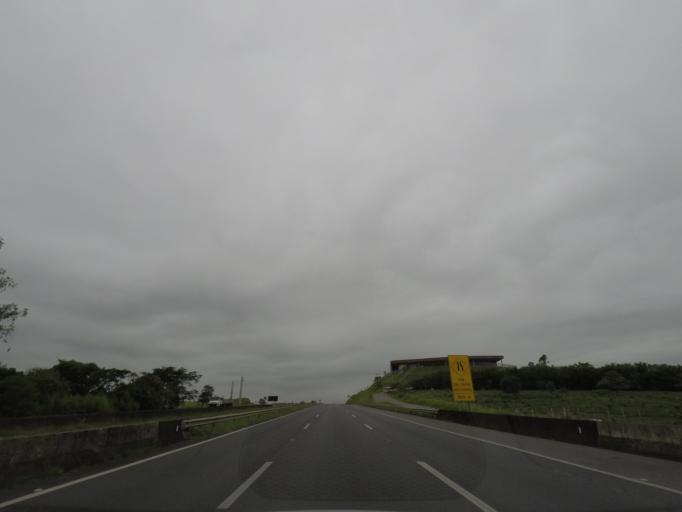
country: BR
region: Sao Paulo
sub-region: Jacarei
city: Jacarei
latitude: -23.2664
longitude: -46.0626
